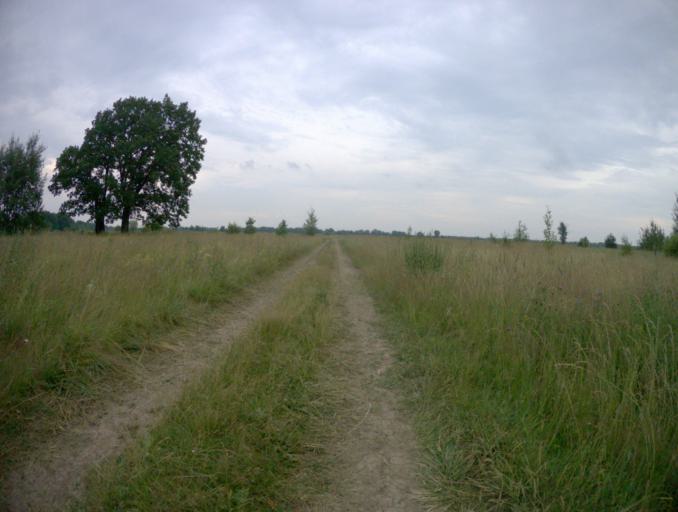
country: RU
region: Vladimir
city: Galitsy
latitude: 56.1809
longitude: 42.8091
